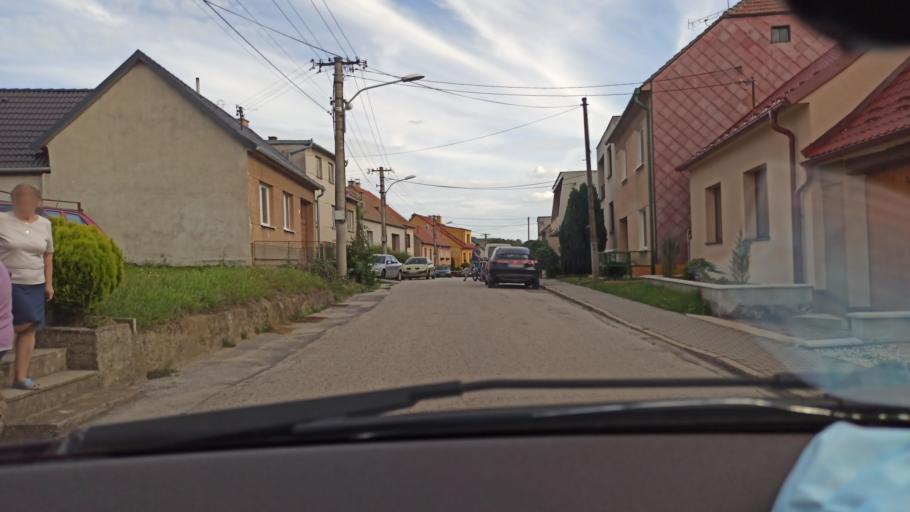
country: SK
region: Trnavsky
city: Gbely
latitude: 48.6778
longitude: 17.2026
